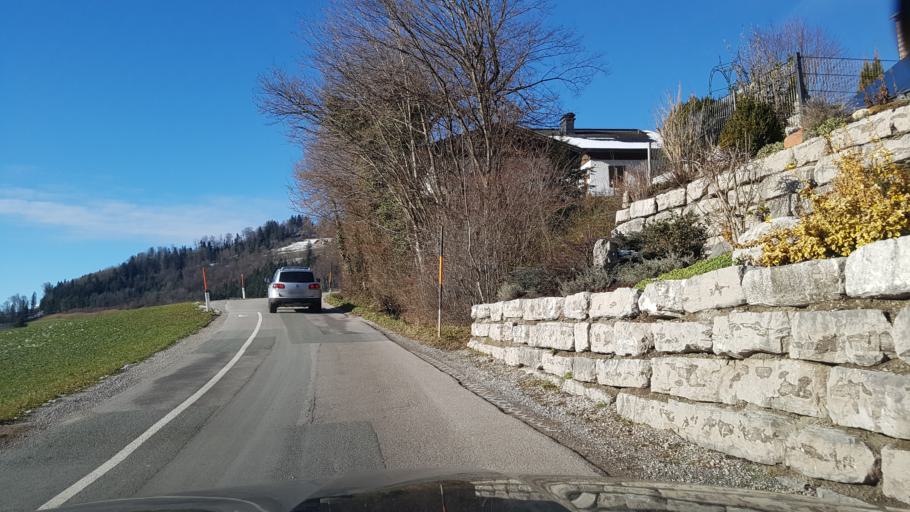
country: AT
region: Salzburg
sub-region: Politischer Bezirk Salzburg-Umgebung
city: Koppl
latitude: 47.7752
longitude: 13.1246
